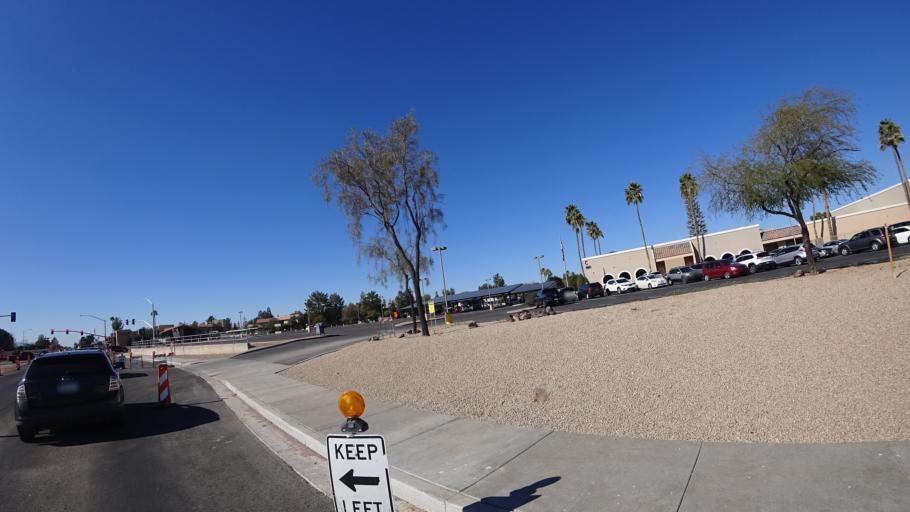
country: US
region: Arizona
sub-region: Maricopa County
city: Sun City
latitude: 33.6527
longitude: -112.2777
